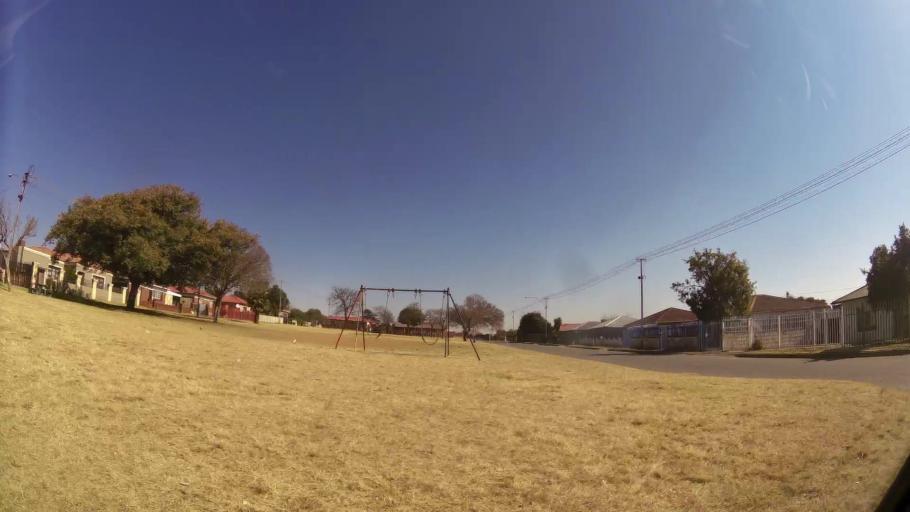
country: ZA
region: Gauteng
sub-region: City of Johannesburg Metropolitan Municipality
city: Johannesburg
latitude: -26.2493
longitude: 28.0870
